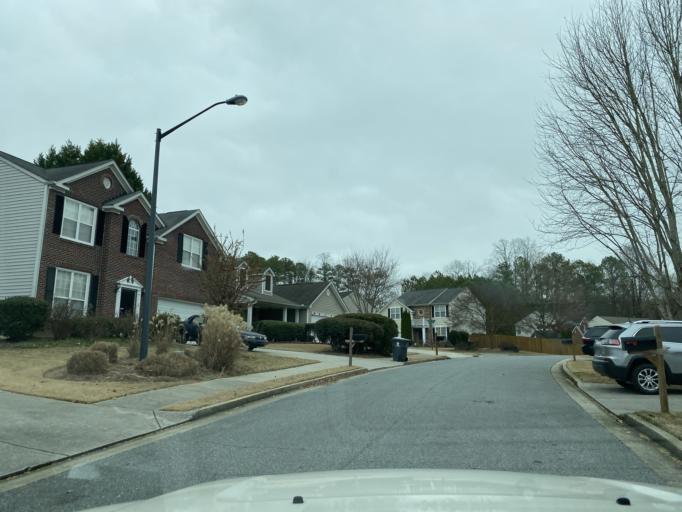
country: US
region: Georgia
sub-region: Cobb County
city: Fair Oaks
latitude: 33.9114
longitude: -84.5644
